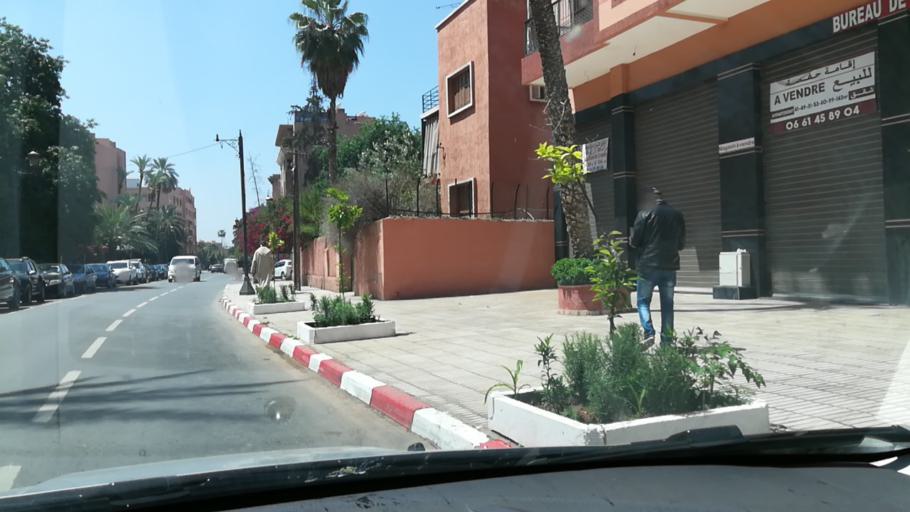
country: MA
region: Marrakech-Tensift-Al Haouz
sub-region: Marrakech
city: Marrakesh
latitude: 31.6316
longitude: -8.0038
